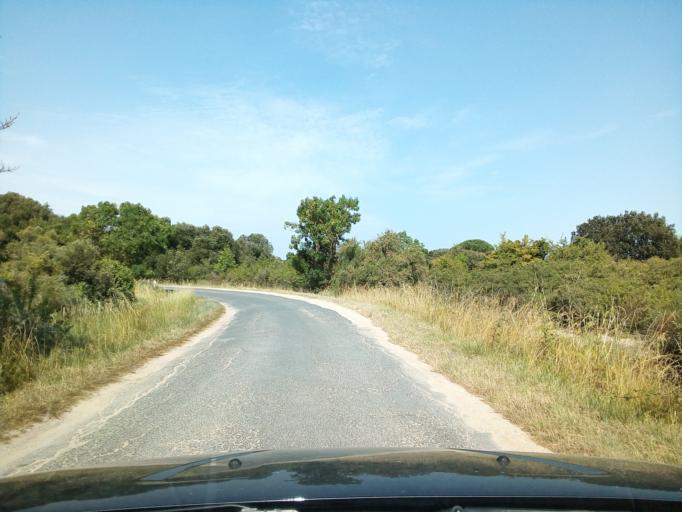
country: FR
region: Poitou-Charentes
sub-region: Departement de la Charente-Maritime
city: Boyard-Ville
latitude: 45.9577
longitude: -1.2613
